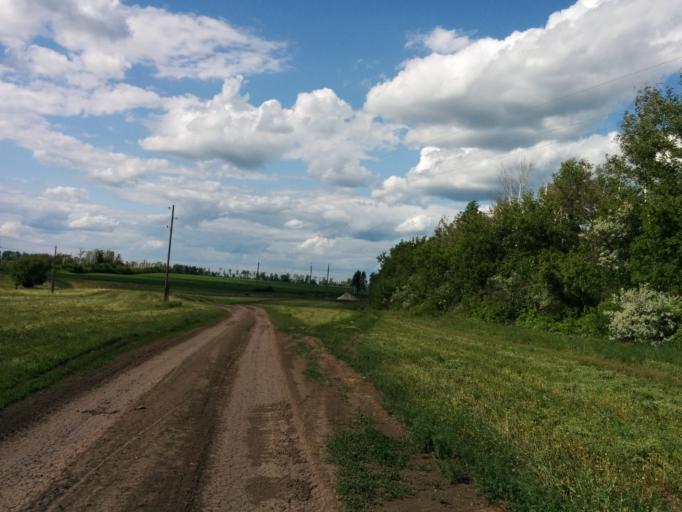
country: RU
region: Tambov
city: Tambov
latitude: 52.7933
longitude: 41.3829
